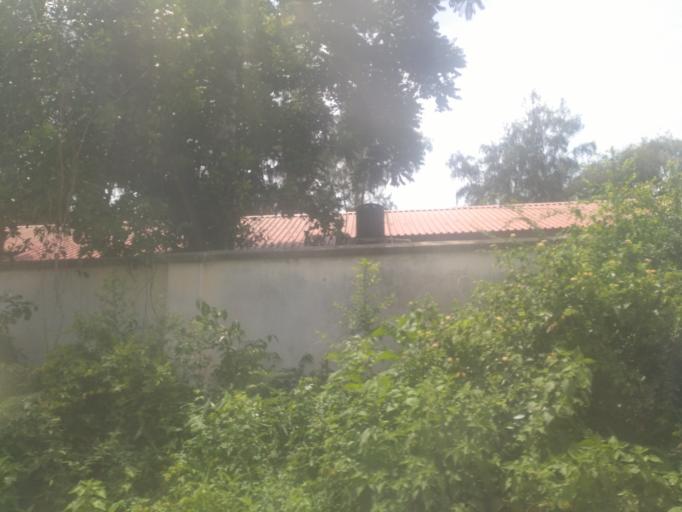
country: TZ
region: Zanzibar Urban/West
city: Zanzibar
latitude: -6.2142
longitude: 39.2079
